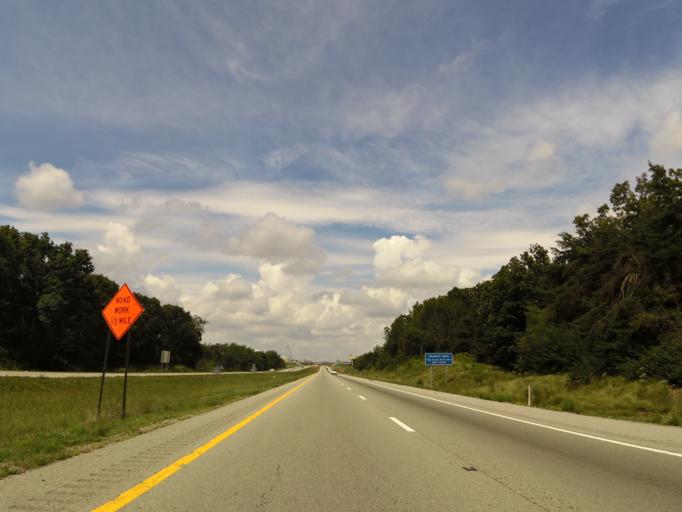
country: US
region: Tennessee
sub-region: Cumberland County
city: Crossville
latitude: 35.9772
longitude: -85.0050
